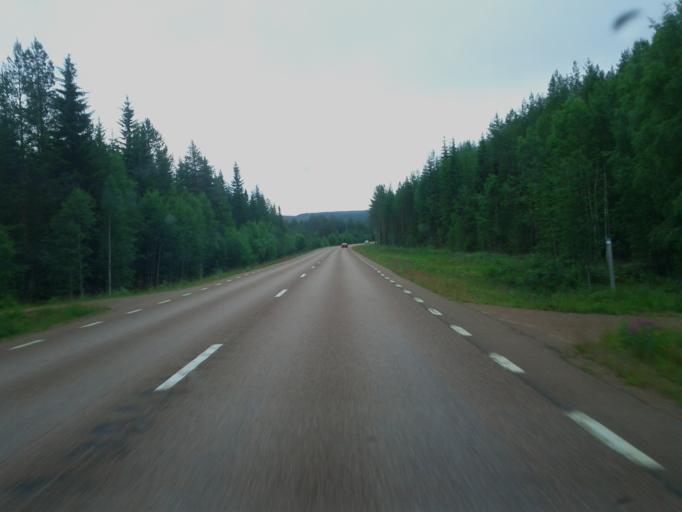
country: SE
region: Dalarna
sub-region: Alvdalens Kommun
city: AElvdalen
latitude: 61.2752
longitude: 13.7827
